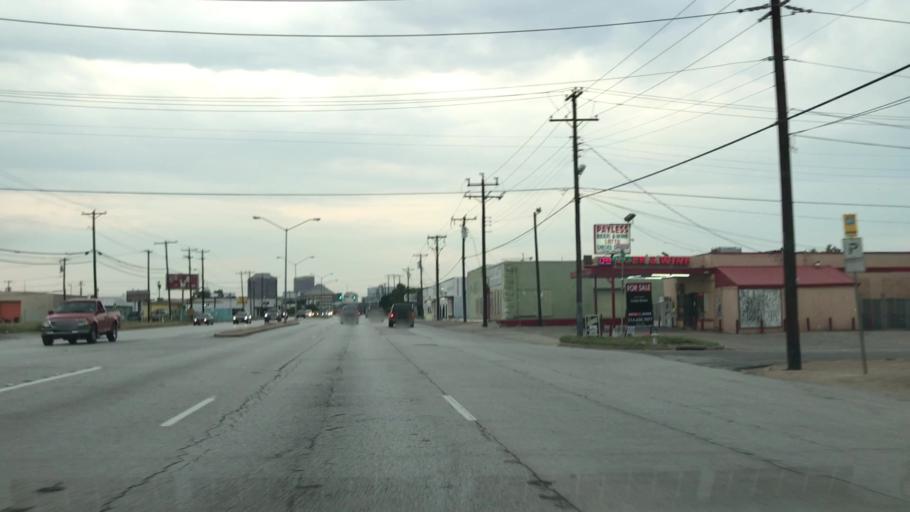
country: US
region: Texas
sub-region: Dallas County
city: Dallas
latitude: 32.7861
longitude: -96.8173
